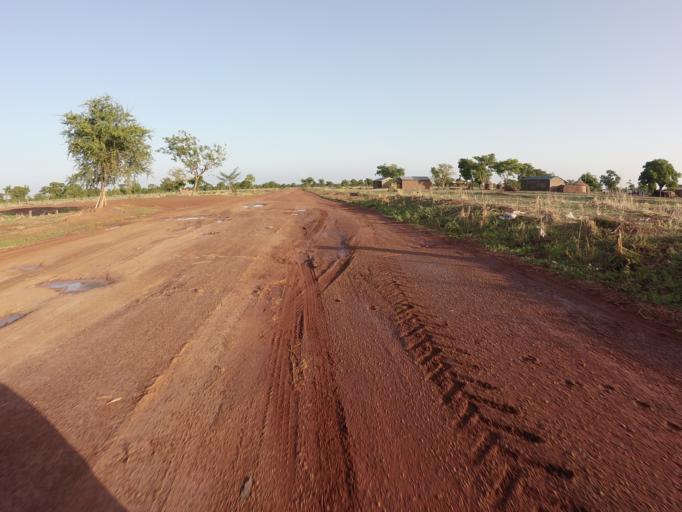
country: TG
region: Savanes
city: Sansanne-Mango
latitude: 10.2954
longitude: -0.0883
